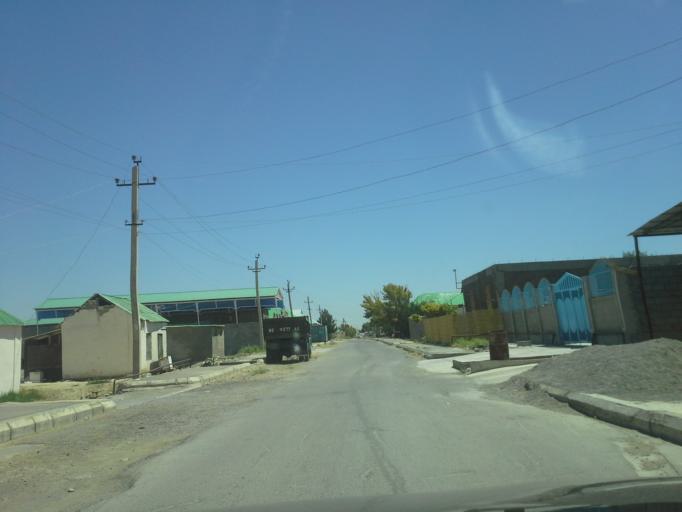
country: TM
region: Ahal
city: Abadan
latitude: 38.0323
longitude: 58.2681
